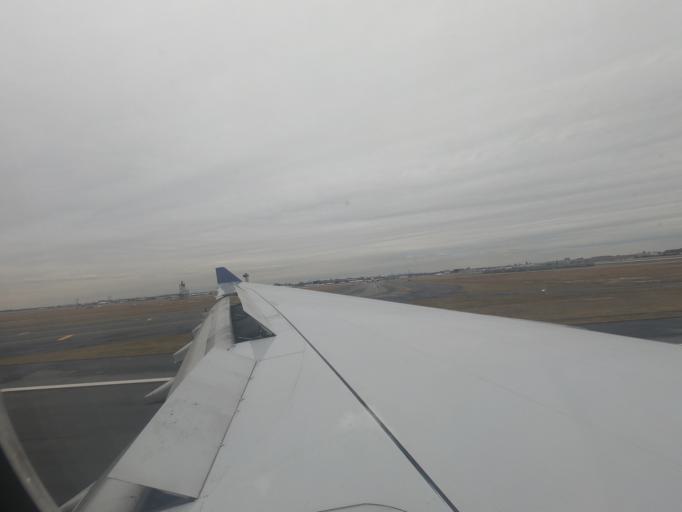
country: US
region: New York
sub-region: Nassau County
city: Inwood
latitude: 40.6396
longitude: -73.7595
